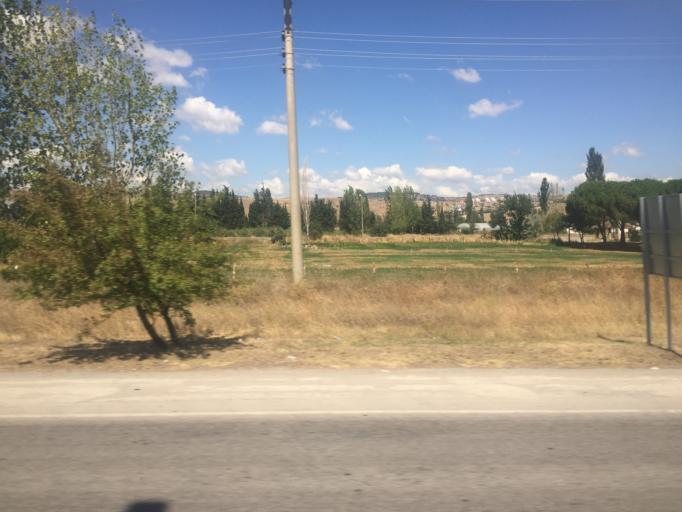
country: TR
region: Balikesir
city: Balikesir
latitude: 39.6837
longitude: 27.9417
